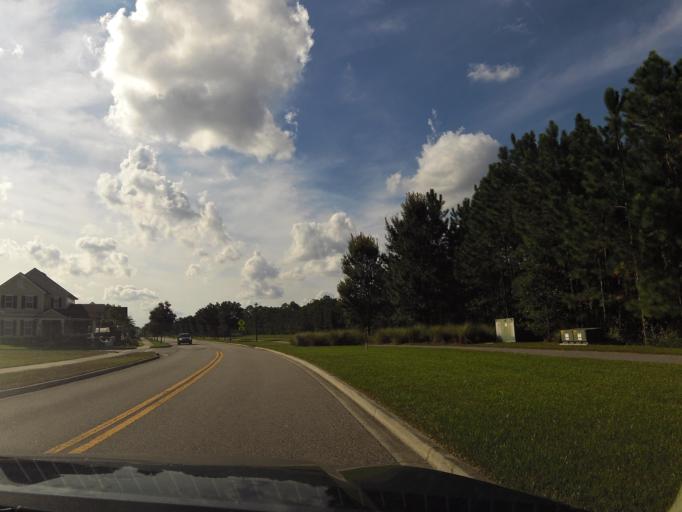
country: US
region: Florida
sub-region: Clay County
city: Green Cove Springs
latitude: 29.9303
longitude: -81.5086
